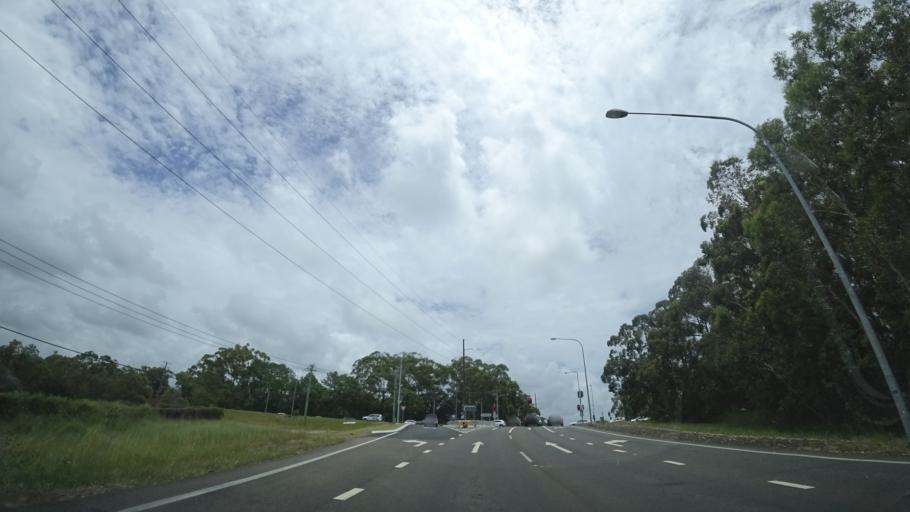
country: AU
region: Queensland
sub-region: Sunshine Coast
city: Mooloolaba
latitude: -26.6763
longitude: 153.0968
